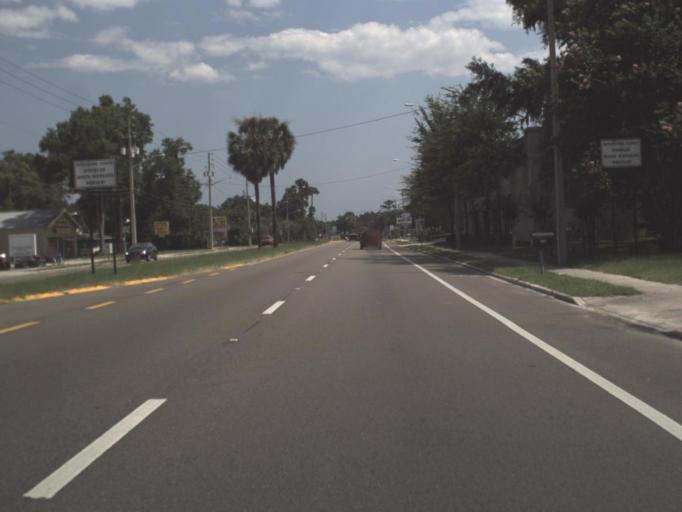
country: US
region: Florida
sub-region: Alachua County
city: Gainesville
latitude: 29.6931
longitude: -82.3389
